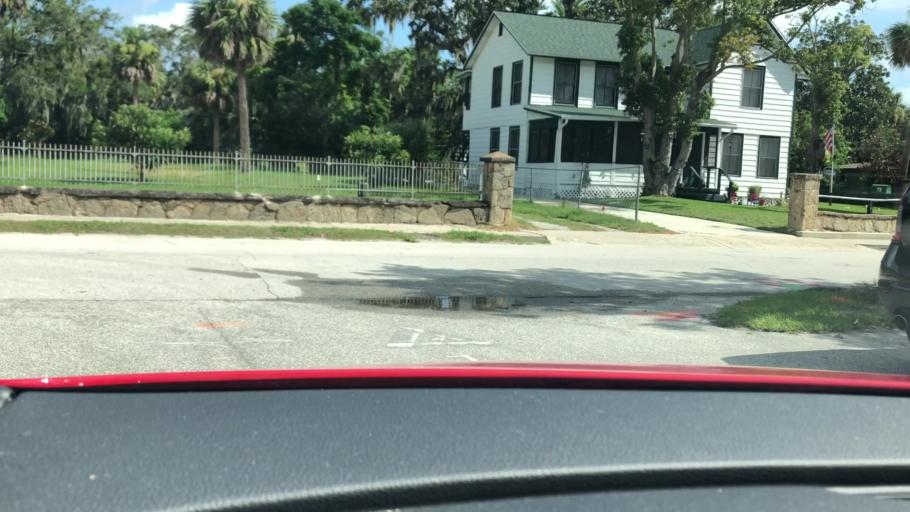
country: US
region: Florida
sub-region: Volusia County
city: Ormond Beach
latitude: 29.2853
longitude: -81.0581
